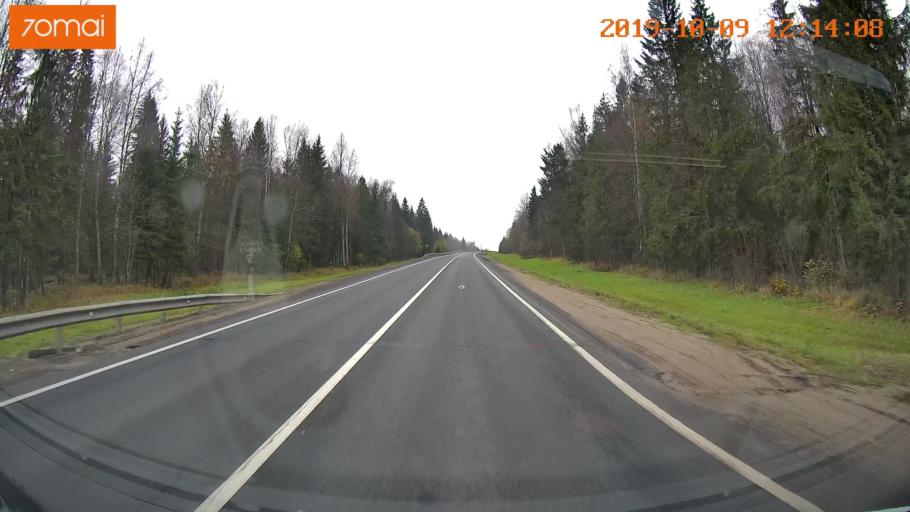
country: RU
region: Jaroslavl
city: Prechistoye
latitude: 58.5002
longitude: 40.3406
